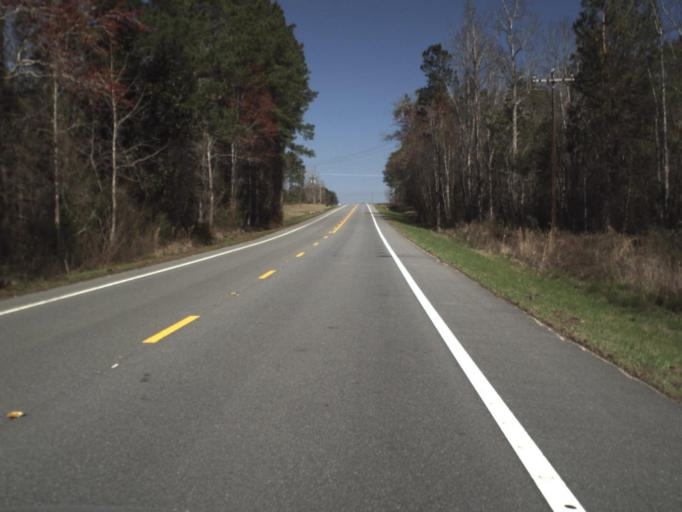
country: US
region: Florida
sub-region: Jackson County
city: Sneads
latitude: 30.6128
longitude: -85.0298
